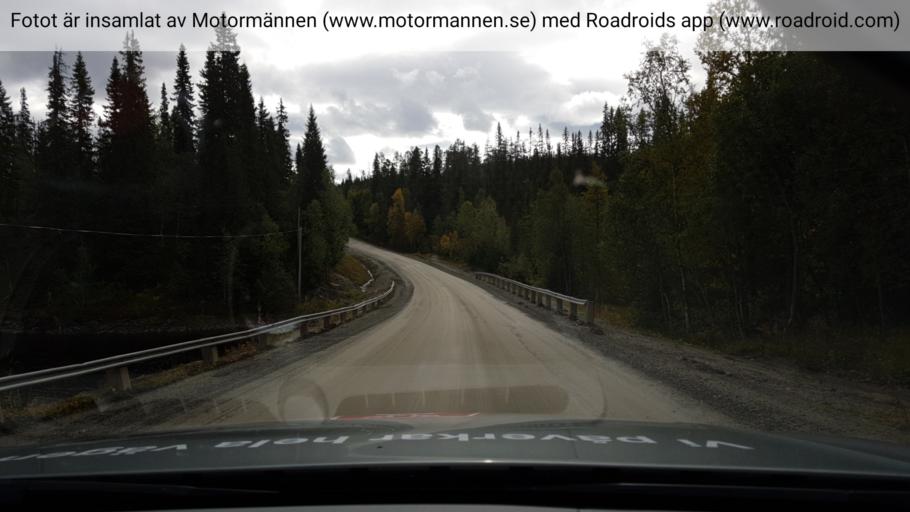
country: SE
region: Jaemtland
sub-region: Are Kommun
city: Are
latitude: 63.7203
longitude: 12.6079
